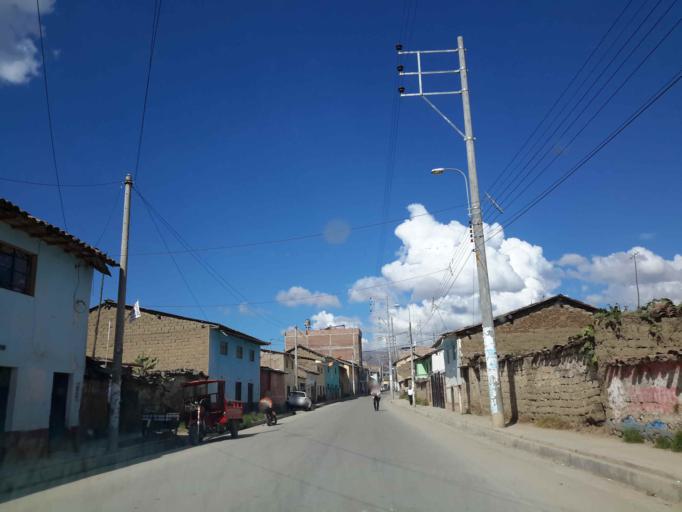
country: PE
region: Apurimac
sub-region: Provincia de Andahuaylas
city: Talavera
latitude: -13.6530
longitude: -73.4323
